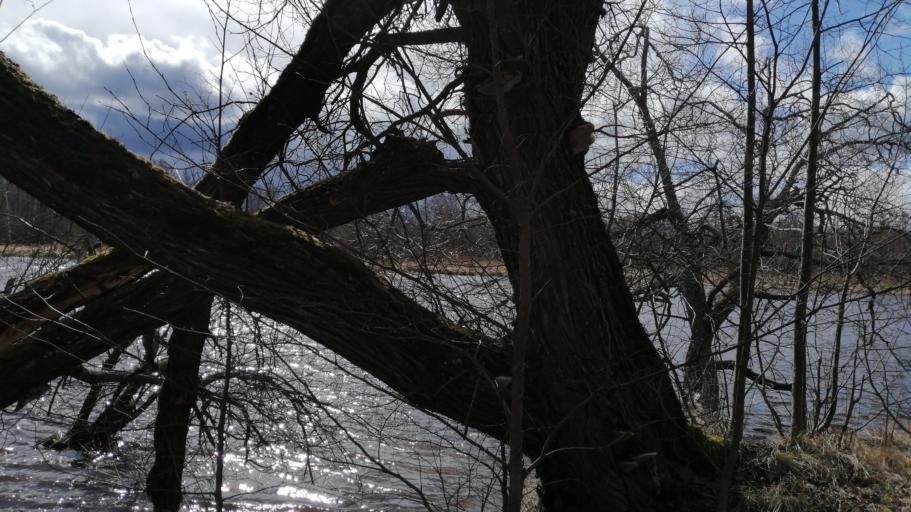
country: EE
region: Tartu
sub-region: Alatskivi vald
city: Kallaste
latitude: 58.3837
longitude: 27.1175
